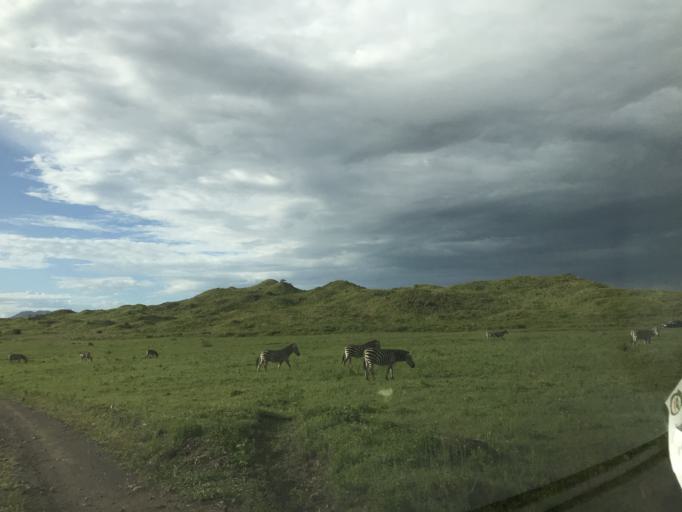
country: TZ
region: Arusha
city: Kingori
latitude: -3.2243
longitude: 36.8830
